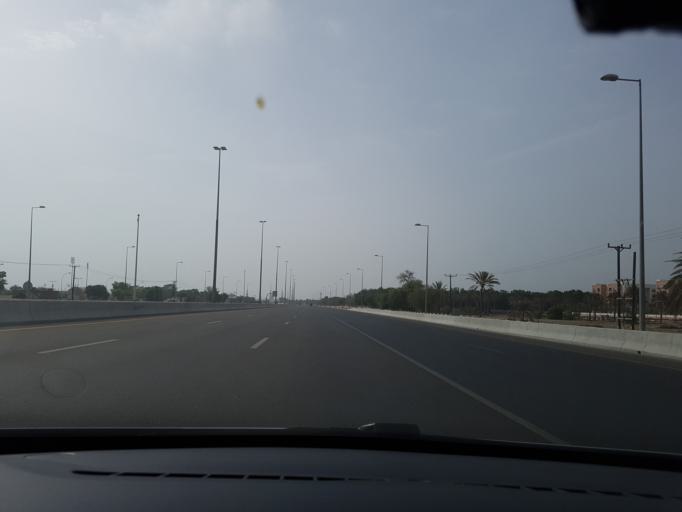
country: OM
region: Al Batinah
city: Al Sohar
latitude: 24.3364
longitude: 56.7363
